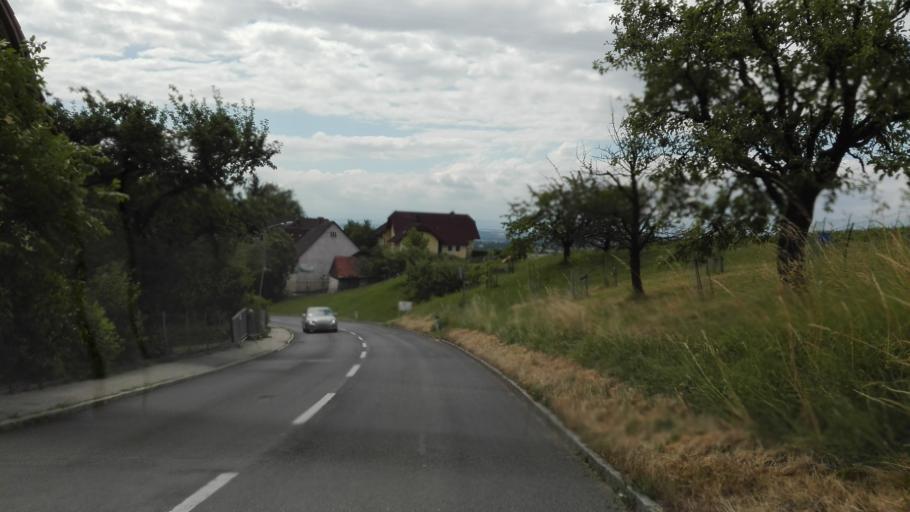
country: AT
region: Upper Austria
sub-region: Politischer Bezirk Perg
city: Perg
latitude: 48.2547
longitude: 14.6271
